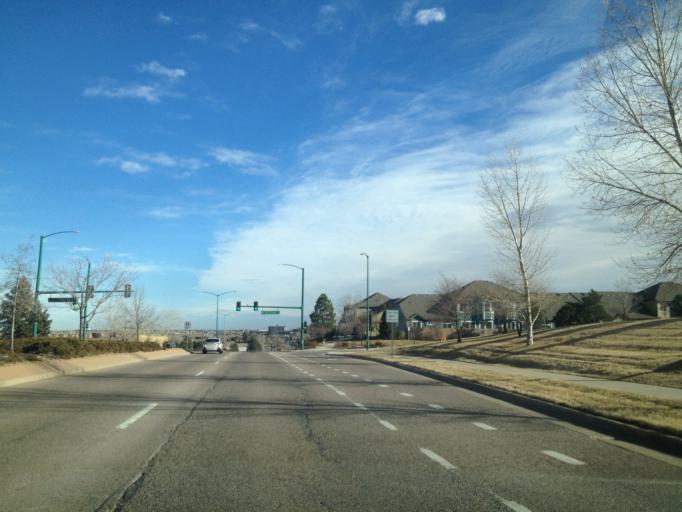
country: US
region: Colorado
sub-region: Boulder County
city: Superior
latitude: 39.9291
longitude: -105.1541
